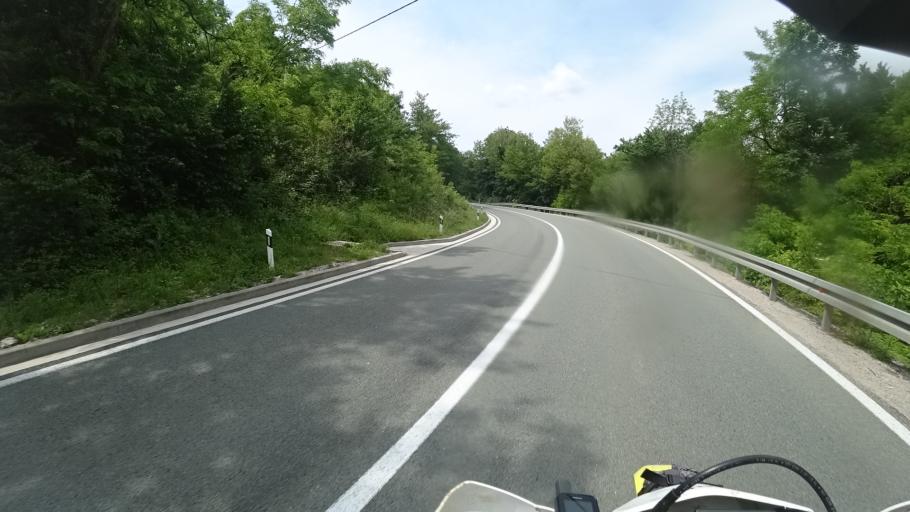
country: BA
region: Federation of Bosnia and Herzegovina
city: Izacic
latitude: 44.8801
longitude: 15.7032
